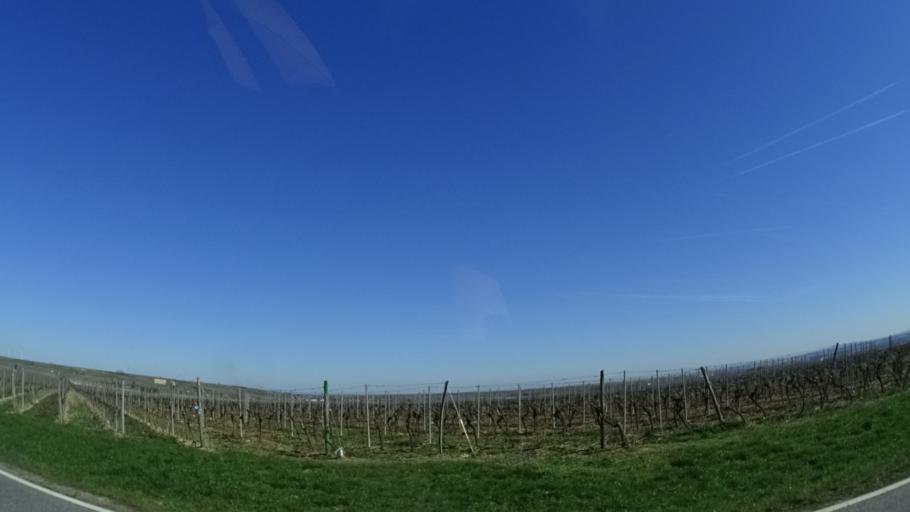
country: DE
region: Rheinland-Pfalz
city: Osthofen
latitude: 49.7110
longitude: 8.3131
